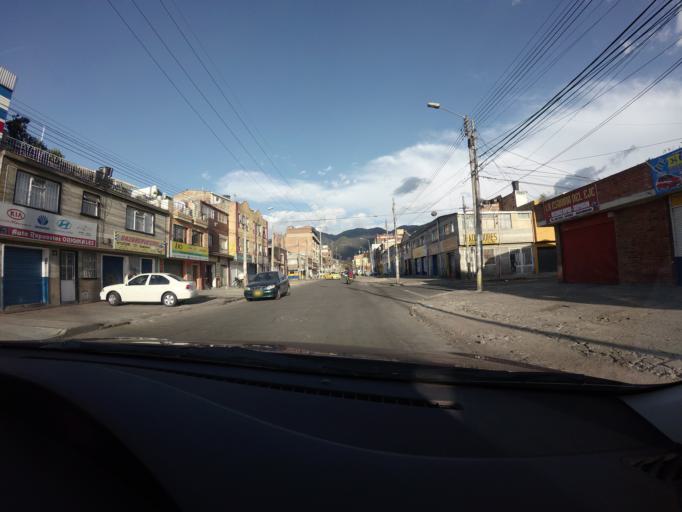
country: CO
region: Bogota D.C.
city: Bogota
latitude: 4.6557
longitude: -74.0728
